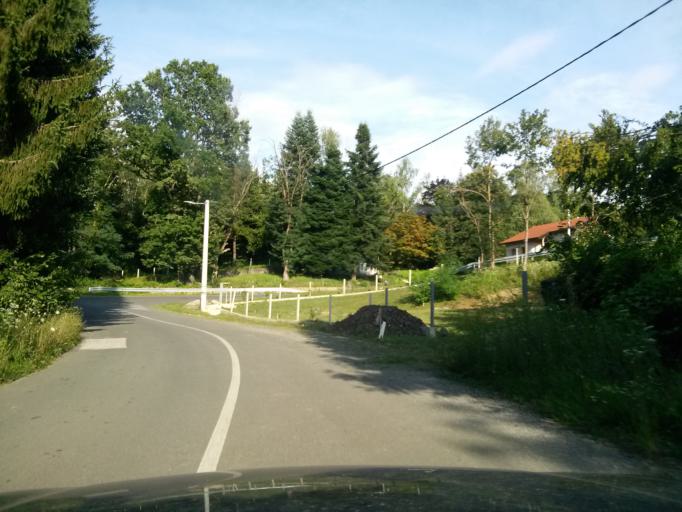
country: HR
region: Sisacko-Moslavacka
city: Gvozd
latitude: 45.5257
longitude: 15.8764
